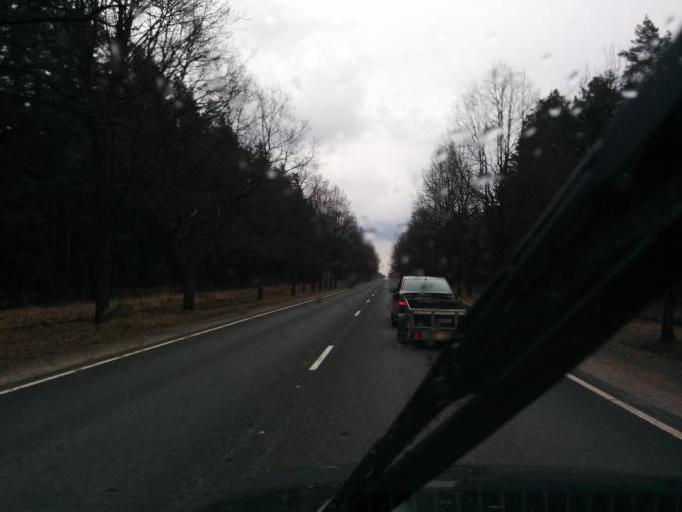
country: LV
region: Ozolnieku
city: Ozolnieki
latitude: 56.7055
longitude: 23.8195
